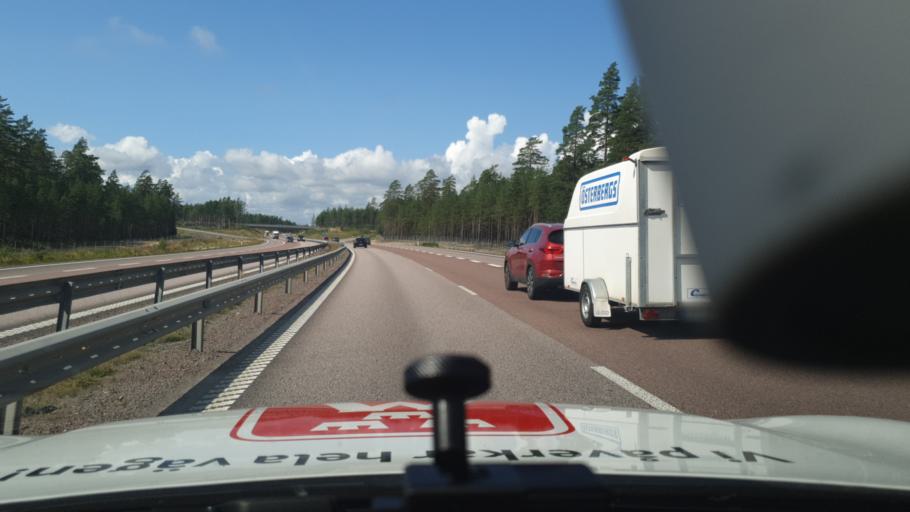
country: SE
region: Vaermland
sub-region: Kils Kommun
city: Kil
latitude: 59.3850
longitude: 13.3462
